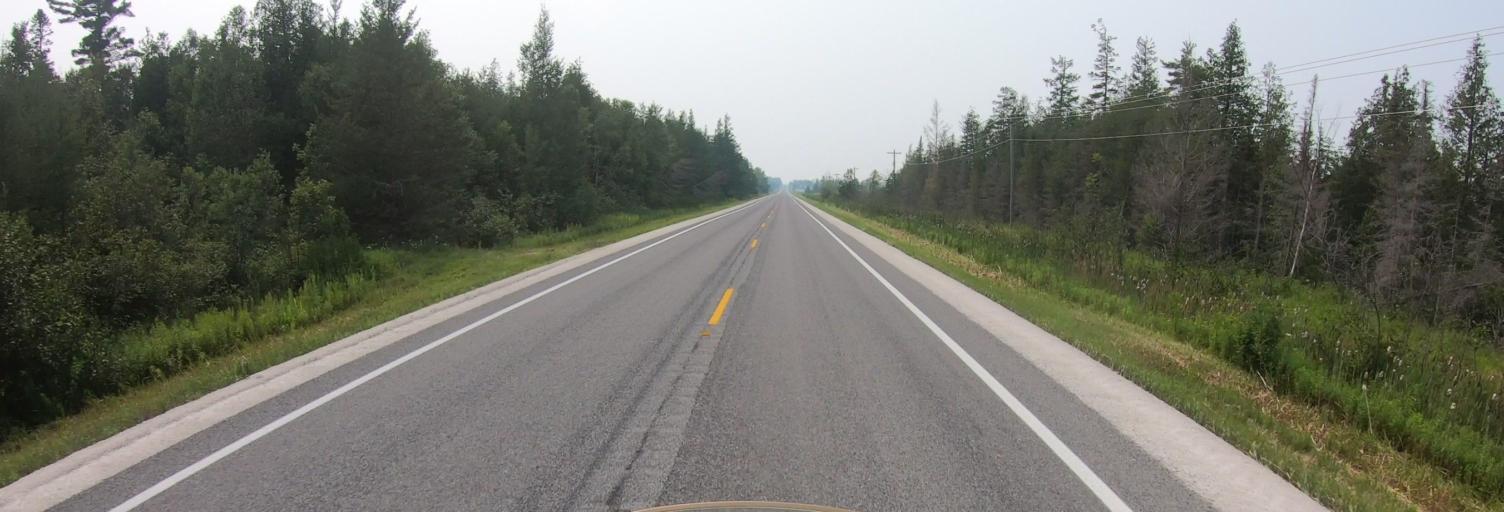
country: US
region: Michigan
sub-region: Chippewa County
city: Sault Ste. Marie
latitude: 46.0718
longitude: -84.1973
